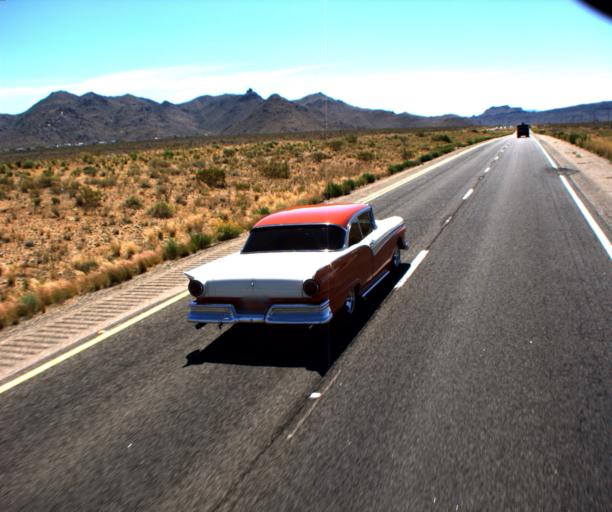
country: US
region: Arizona
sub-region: Mohave County
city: Golden Valley
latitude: 35.2647
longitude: -114.1639
